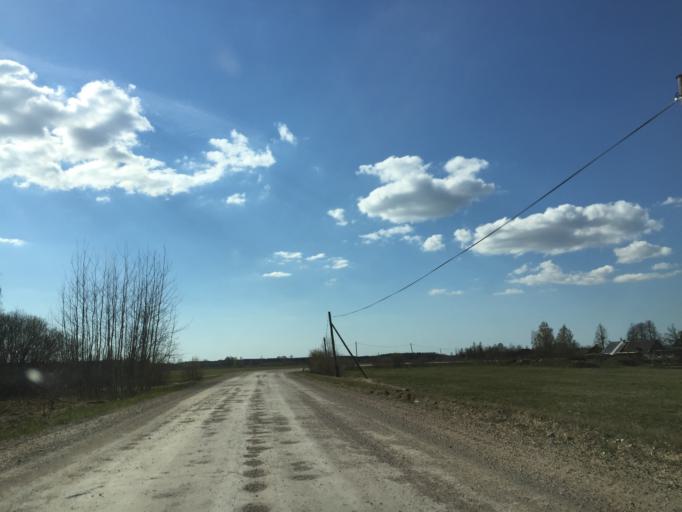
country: LV
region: Saulkrastu
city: Saulkrasti
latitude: 57.3460
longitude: 24.5822
